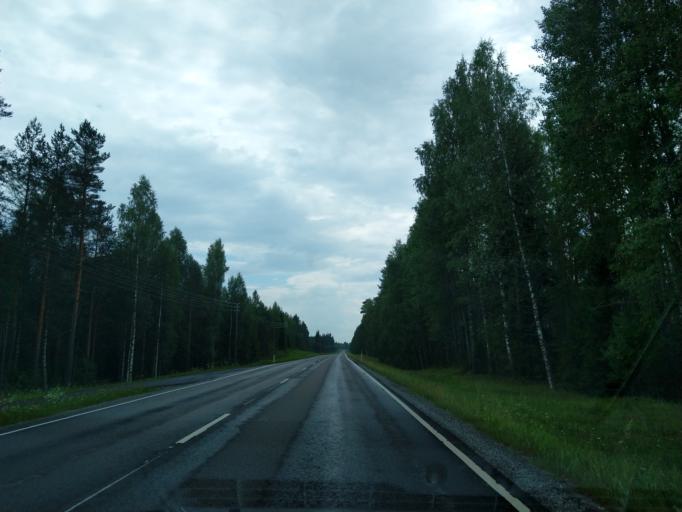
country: FI
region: Southern Savonia
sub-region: Savonlinna
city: Punkaharju
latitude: 61.6502
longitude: 29.4223
